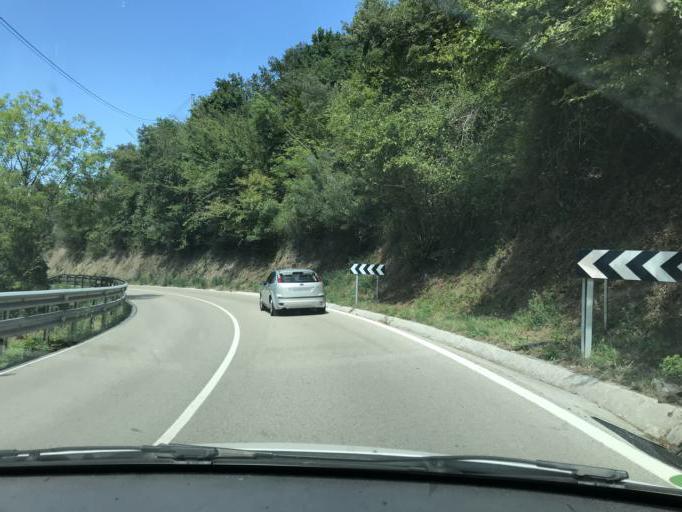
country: ES
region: Cantabria
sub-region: Provincia de Cantabria
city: Cabezon de Liebana
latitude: 43.0942
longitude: -4.5655
